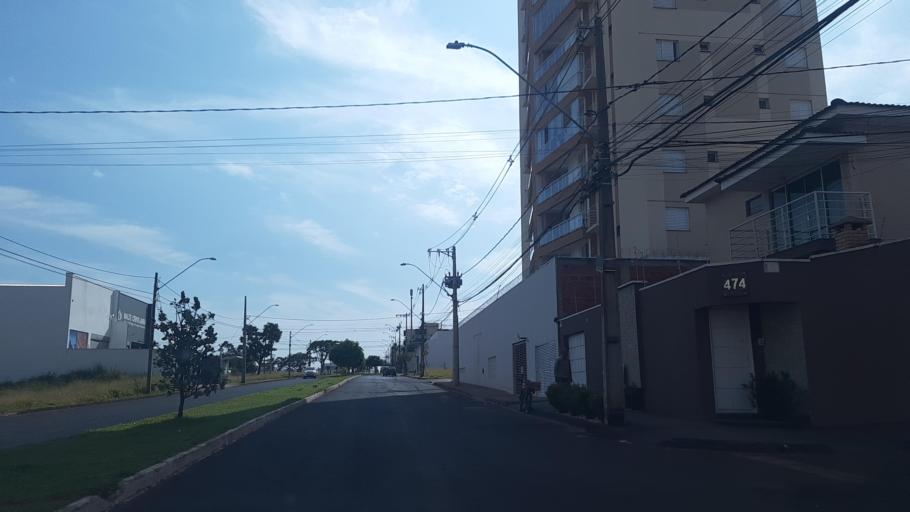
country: BR
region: Minas Gerais
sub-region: Uberlandia
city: Uberlandia
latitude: -18.8733
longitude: -48.2347
